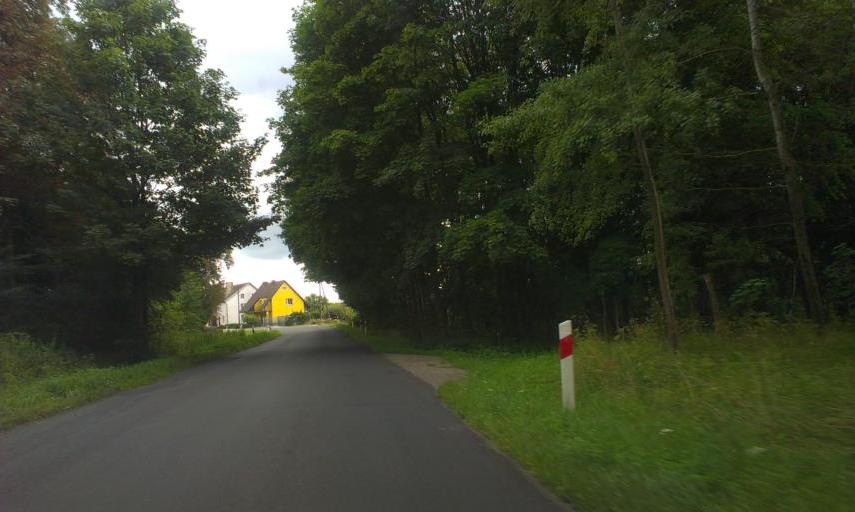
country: PL
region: West Pomeranian Voivodeship
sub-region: Powiat bialogardzki
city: Tychowo
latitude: 53.9390
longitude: 16.2361
